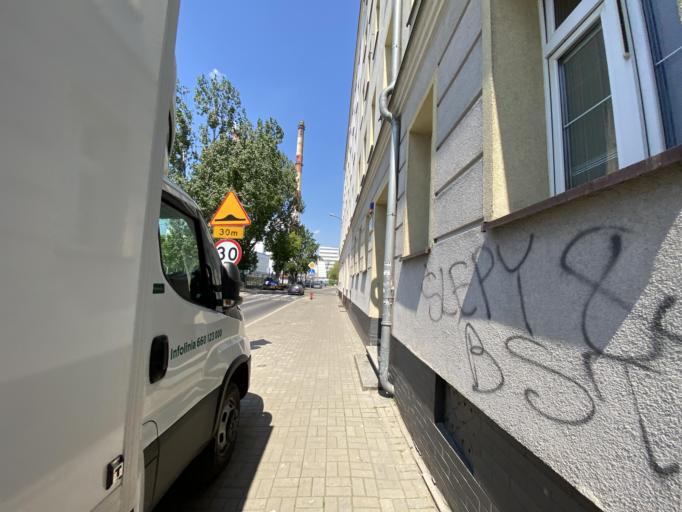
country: PL
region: Lower Silesian Voivodeship
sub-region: Powiat wroclawski
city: Wroclaw
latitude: 51.1214
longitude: 17.0270
